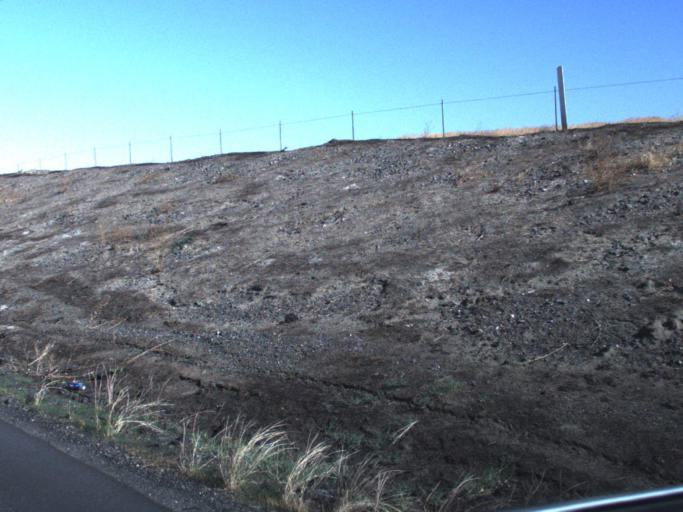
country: US
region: Washington
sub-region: Grant County
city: Desert Aire
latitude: 46.5721
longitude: -119.7274
